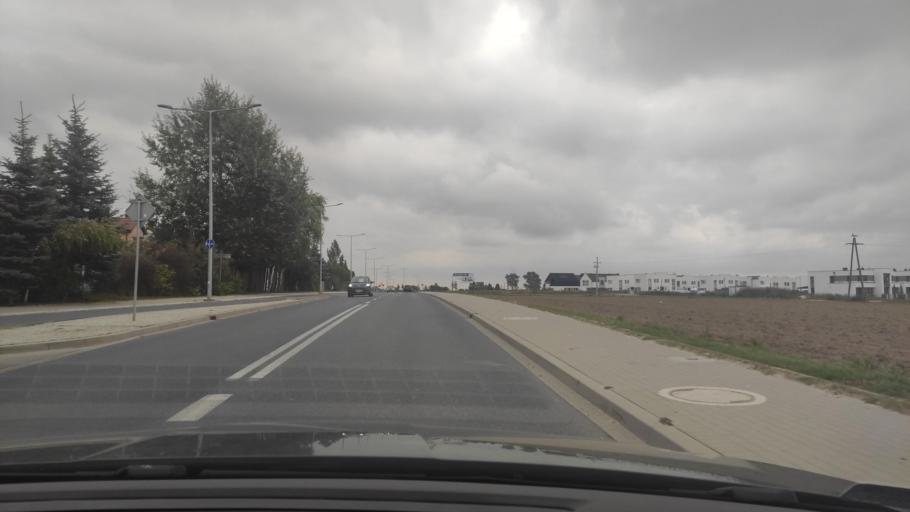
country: PL
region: Greater Poland Voivodeship
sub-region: Powiat poznanski
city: Swarzedz
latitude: 52.3829
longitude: 17.0621
